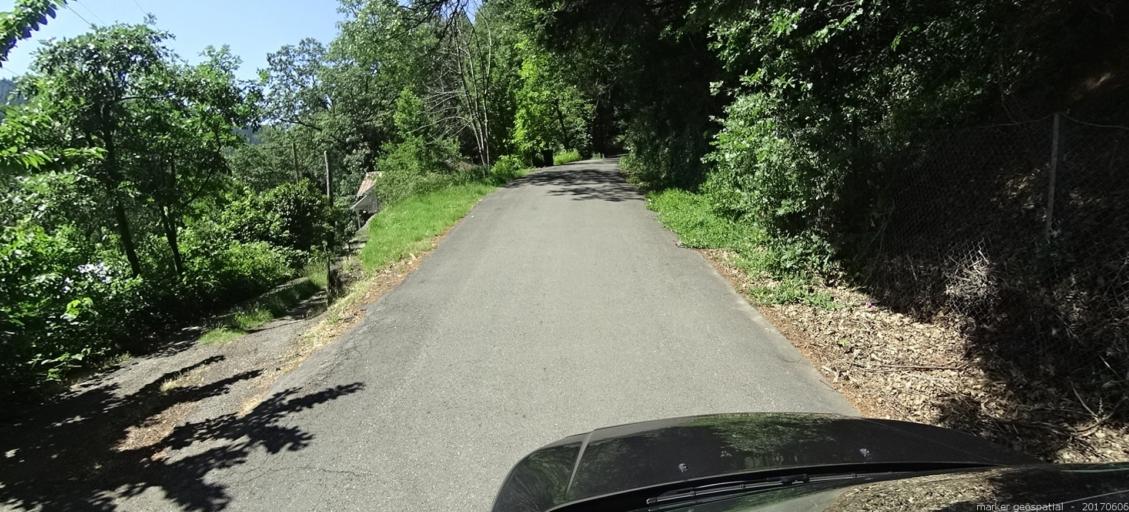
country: US
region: California
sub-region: Siskiyou County
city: Dunsmuir
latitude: 41.2069
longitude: -122.2760
